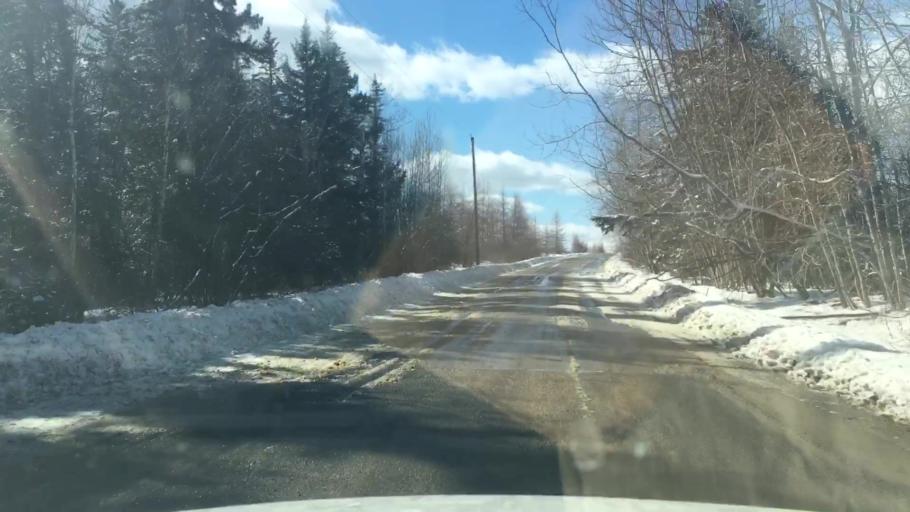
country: US
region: Maine
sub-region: Washington County
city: Machiasport
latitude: 44.6704
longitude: -67.4255
